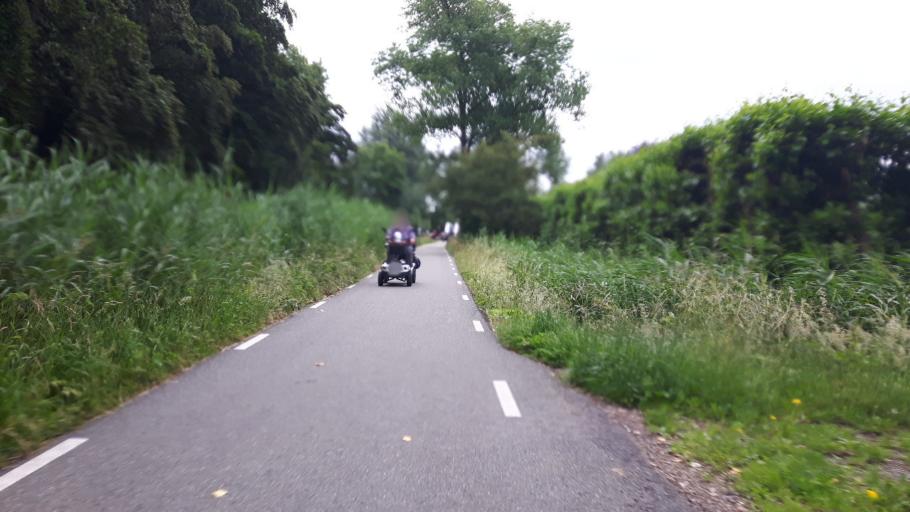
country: NL
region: Utrecht
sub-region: Gemeente Woerden
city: Woerden
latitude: 52.0528
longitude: 4.8996
